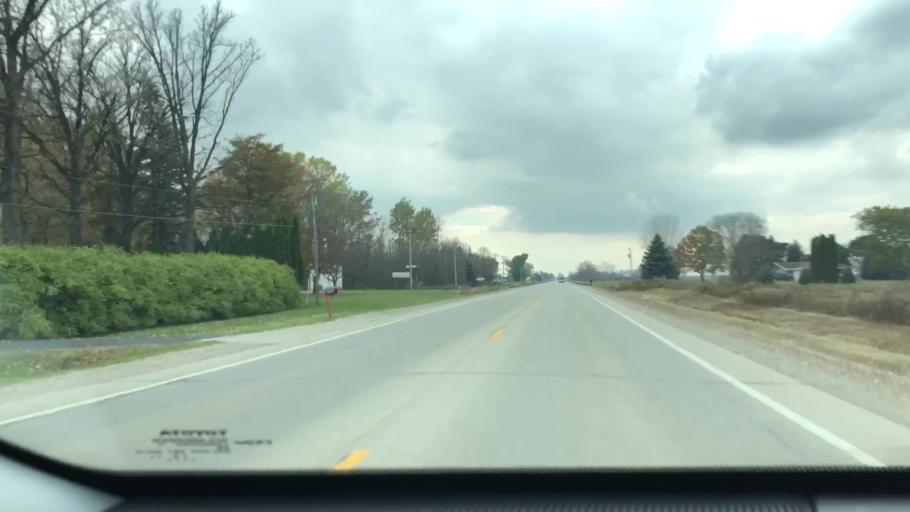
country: US
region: Wisconsin
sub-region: Outagamie County
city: Seymour
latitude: 44.5011
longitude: -88.2742
